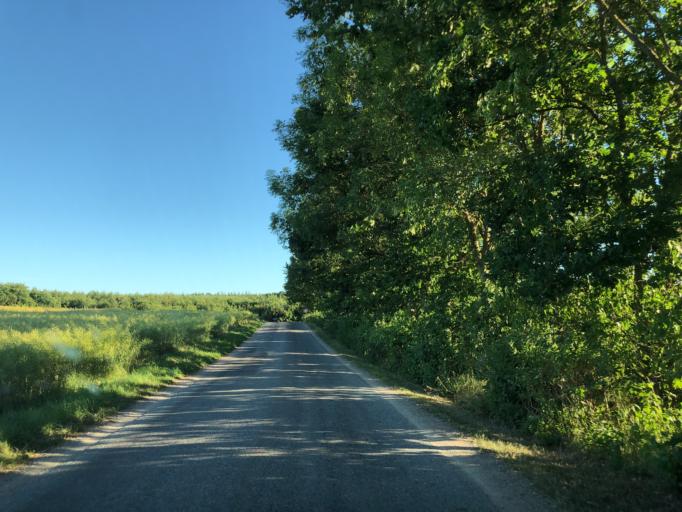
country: DK
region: Central Jutland
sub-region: Horsens Kommune
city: Horsens
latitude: 55.9254
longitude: 9.8654
